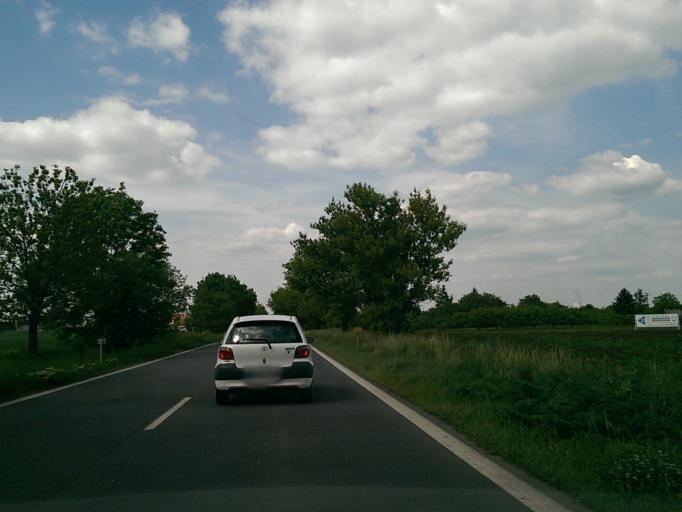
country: CZ
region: Central Bohemia
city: Neratovice
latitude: 50.2487
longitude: 14.4946
